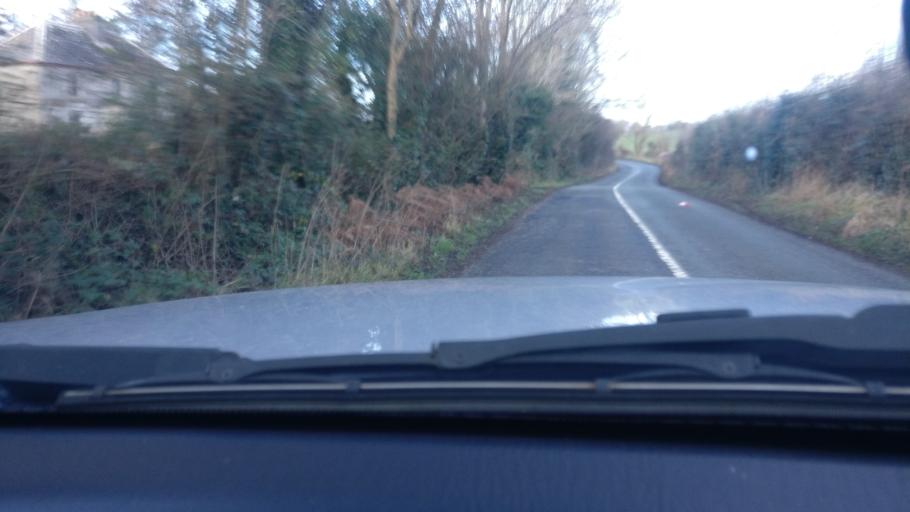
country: IE
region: Connaught
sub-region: County Galway
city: Ballinasloe
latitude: 53.2239
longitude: -8.2914
